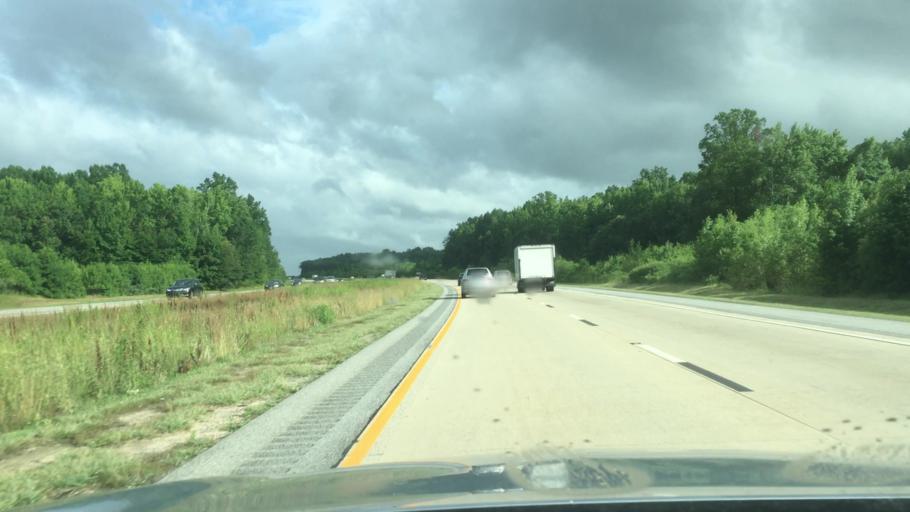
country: US
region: Delaware
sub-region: New Castle County
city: Townsend
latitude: 39.3609
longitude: -75.6539
